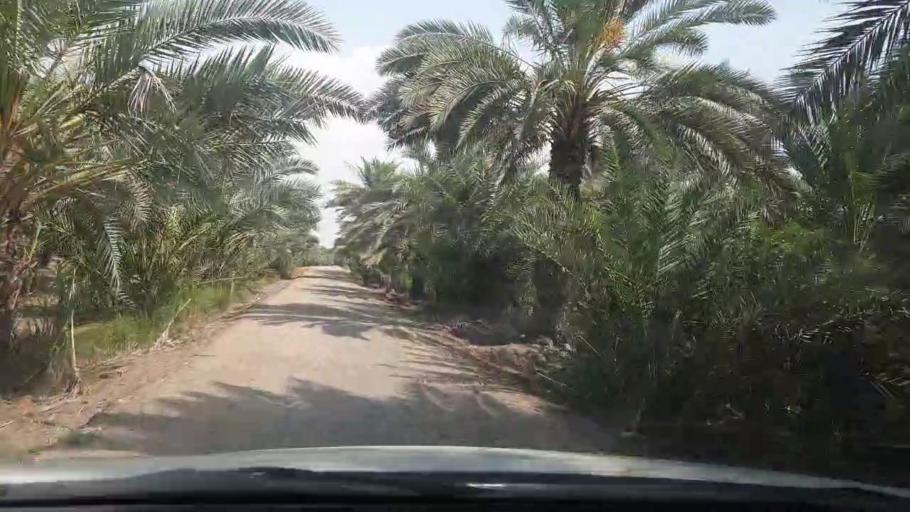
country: PK
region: Sindh
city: Khairpur
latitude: 27.5547
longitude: 68.8430
